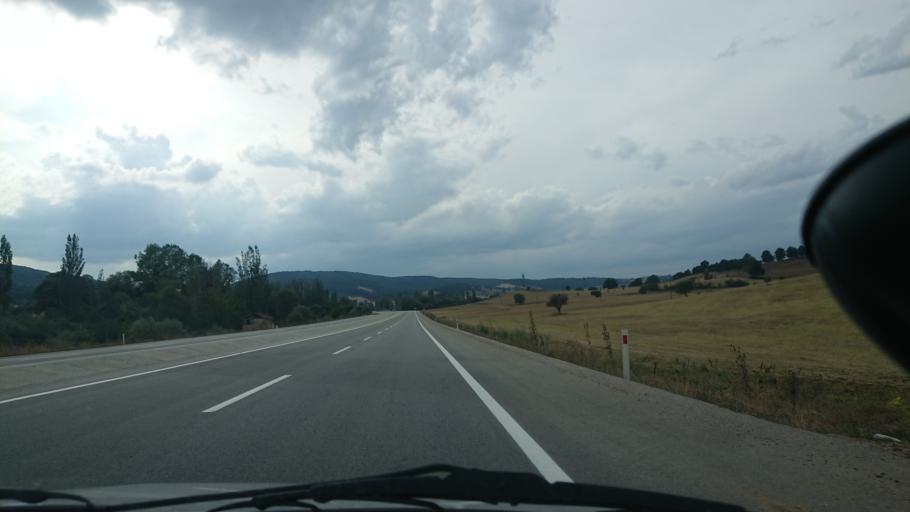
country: TR
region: Kuetahya
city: Cavdarhisar
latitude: 39.1054
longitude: 29.5022
